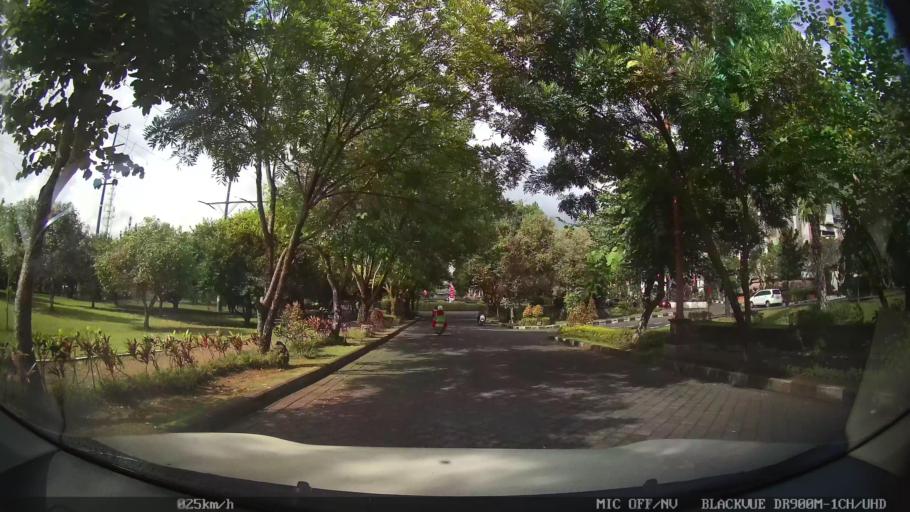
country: ID
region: Bali
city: Banjar Karangsuling
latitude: -8.6037
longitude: 115.1800
